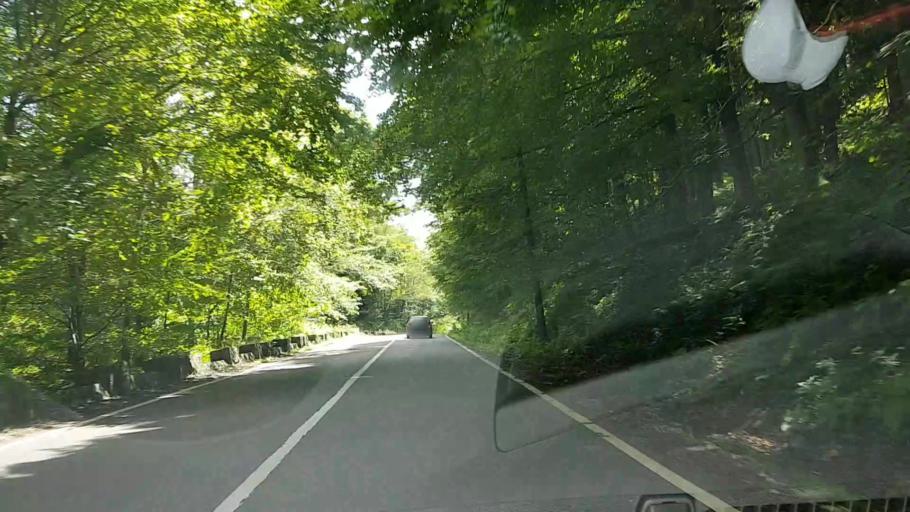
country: RO
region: Suceava
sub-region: Comuna Crucea
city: Crucea
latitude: 47.3061
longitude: 25.6267
